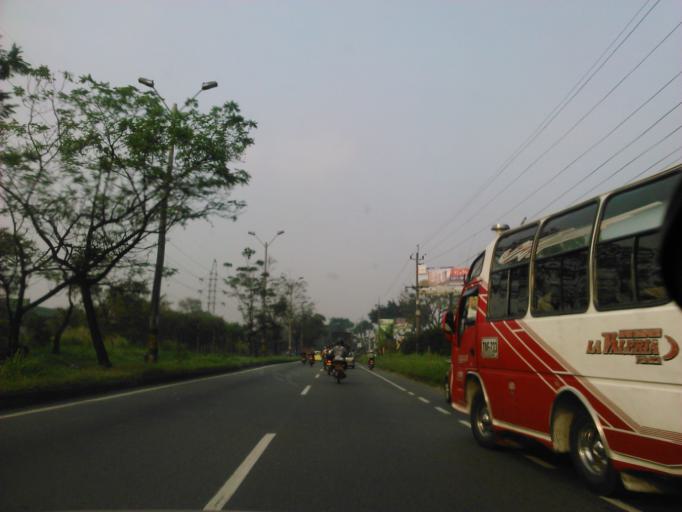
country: CO
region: Antioquia
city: Envigado
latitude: 6.1869
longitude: -75.5860
